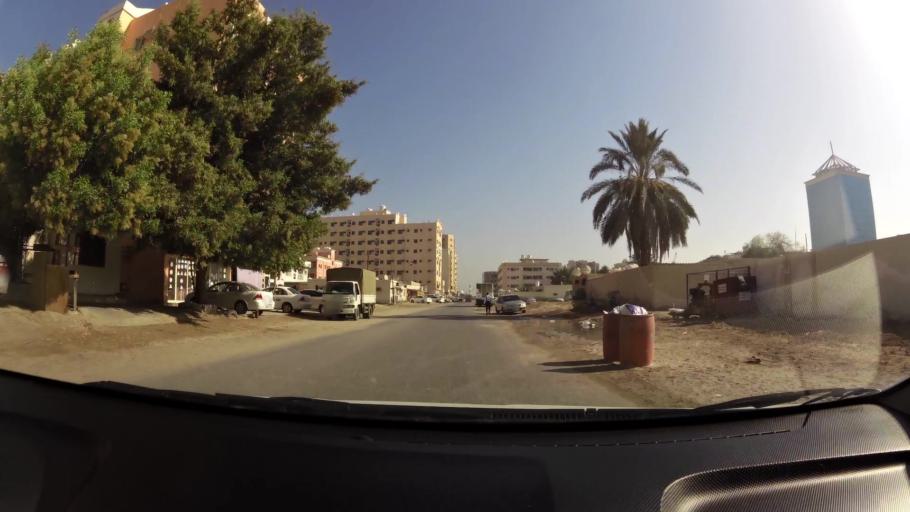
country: AE
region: Ajman
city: Ajman
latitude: 25.4168
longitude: 55.4507
